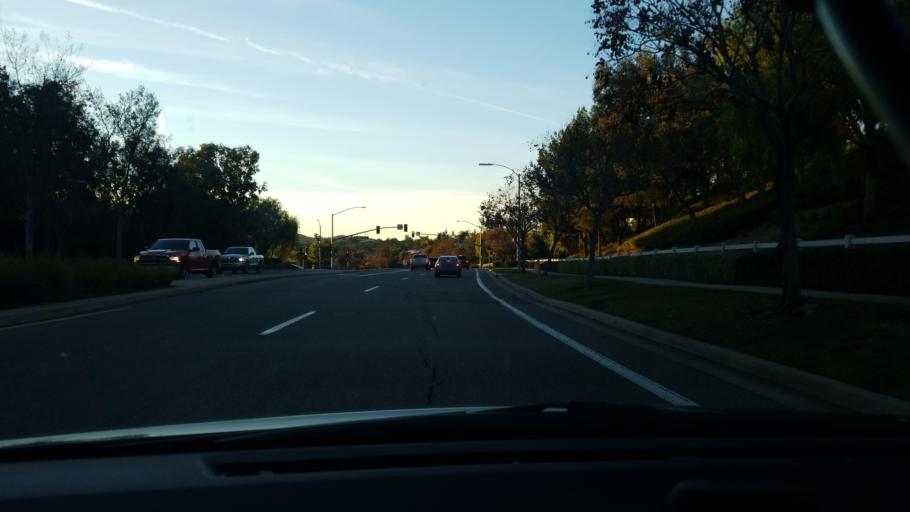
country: US
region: California
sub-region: Riverside County
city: Temecula
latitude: 33.4875
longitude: -117.0940
